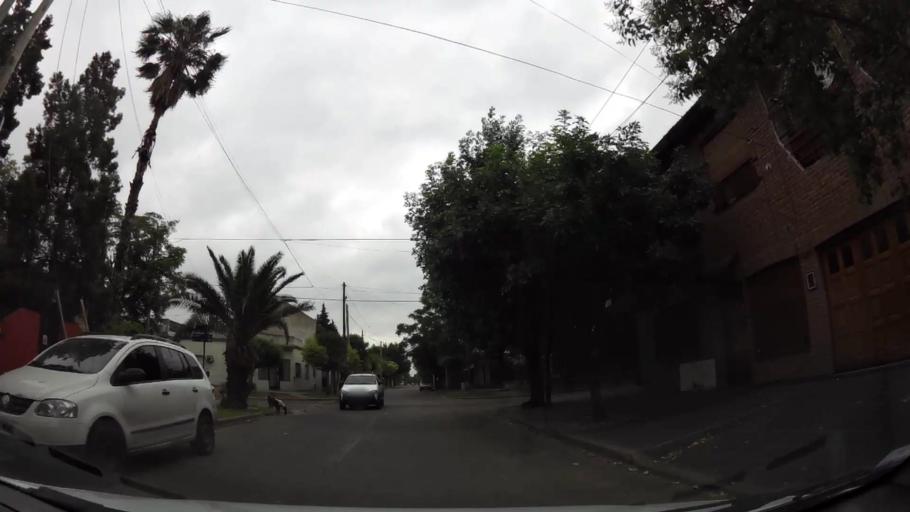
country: AR
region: Buenos Aires
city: San Justo
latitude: -34.7069
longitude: -58.5181
